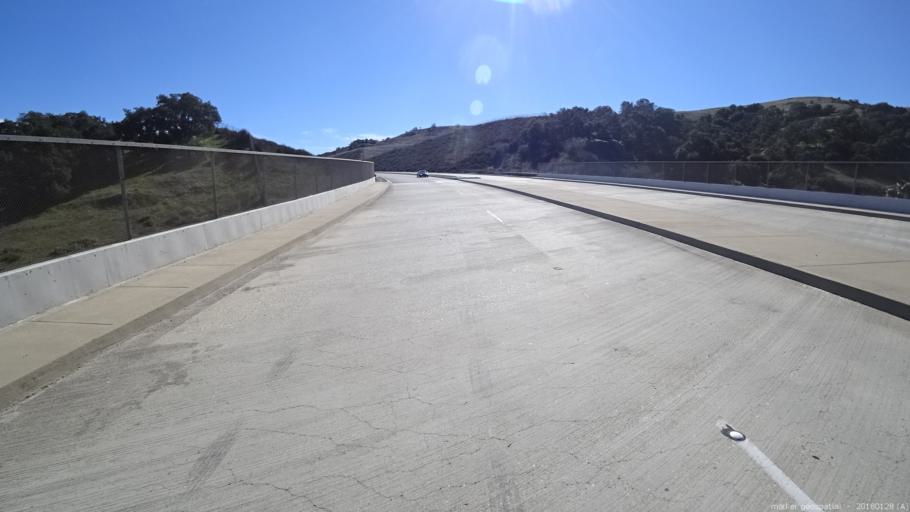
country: US
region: California
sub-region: San Bernardino County
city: Chino Hills
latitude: 34.0191
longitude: -117.7719
